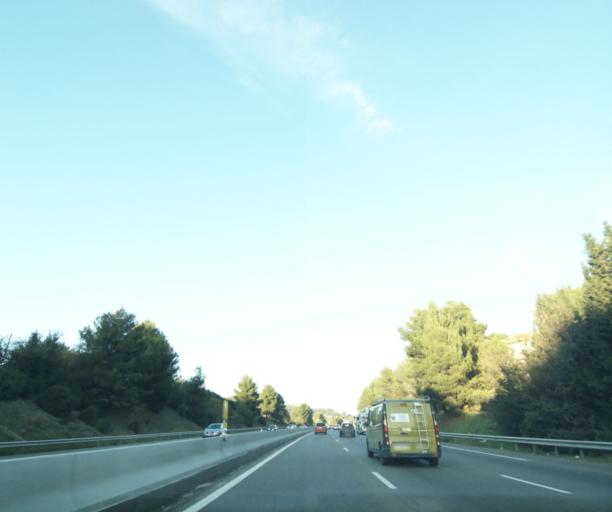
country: FR
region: Provence-Alpes-Cote d'Azur
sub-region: Departement des Bouches-du-Rhone
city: Roquevaire
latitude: 43.3413
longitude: 5.6101
